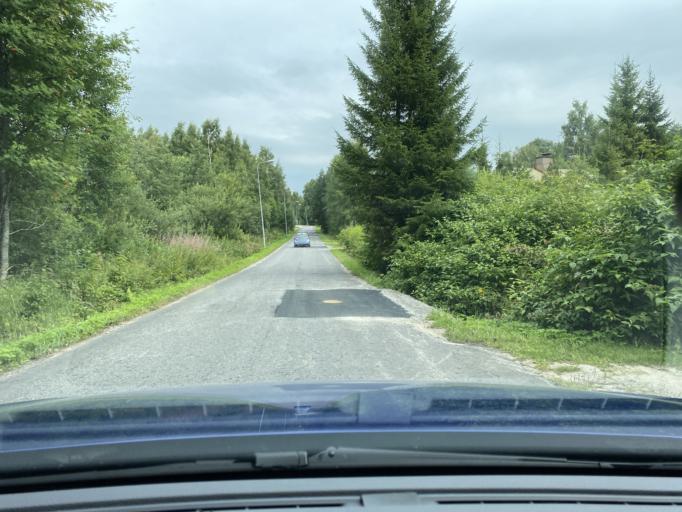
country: FI
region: Pirkanmaa
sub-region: Ylae-Pirkanmaa
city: Maenttae
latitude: 62.0255
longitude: 24.7151
